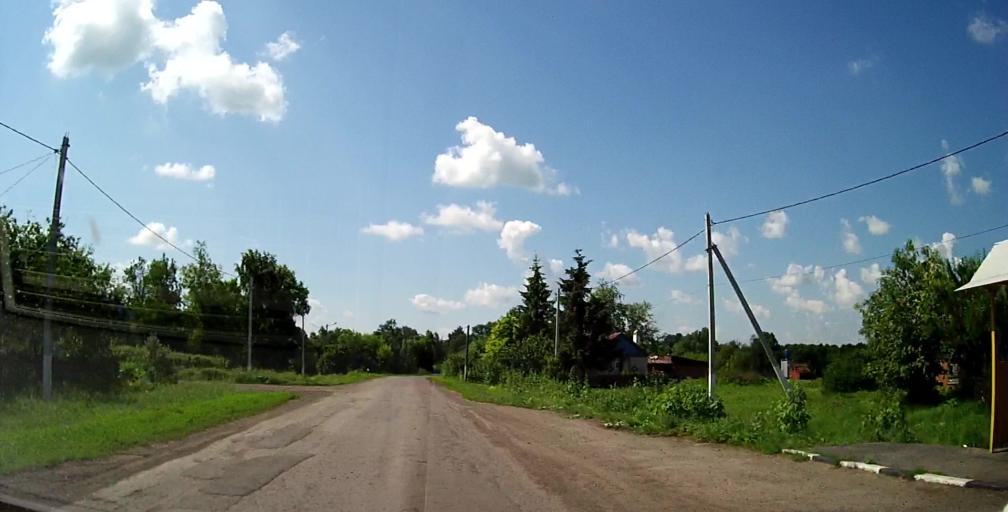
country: RU
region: Lipetsk
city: Chaplygin
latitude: 53.3732
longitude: 39.9170
